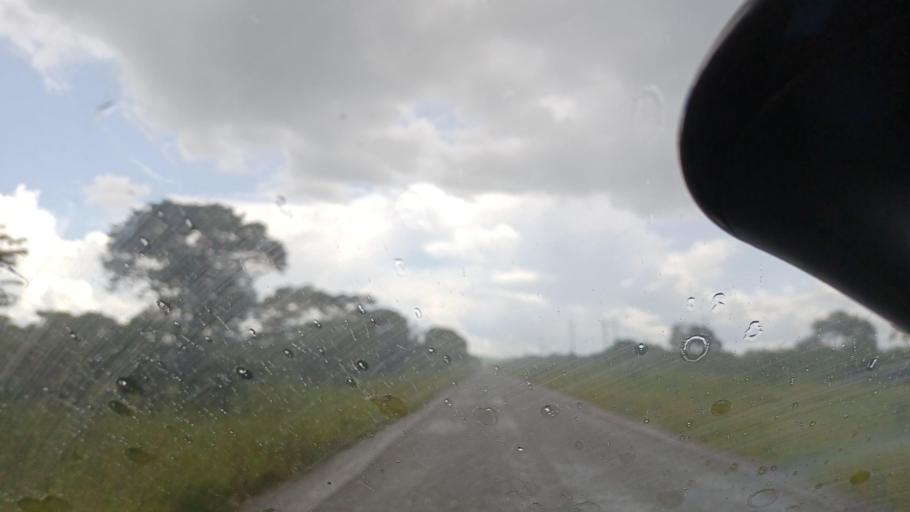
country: ZM
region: North-Western
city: Kasempa
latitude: -13.0991
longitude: 25.9007
